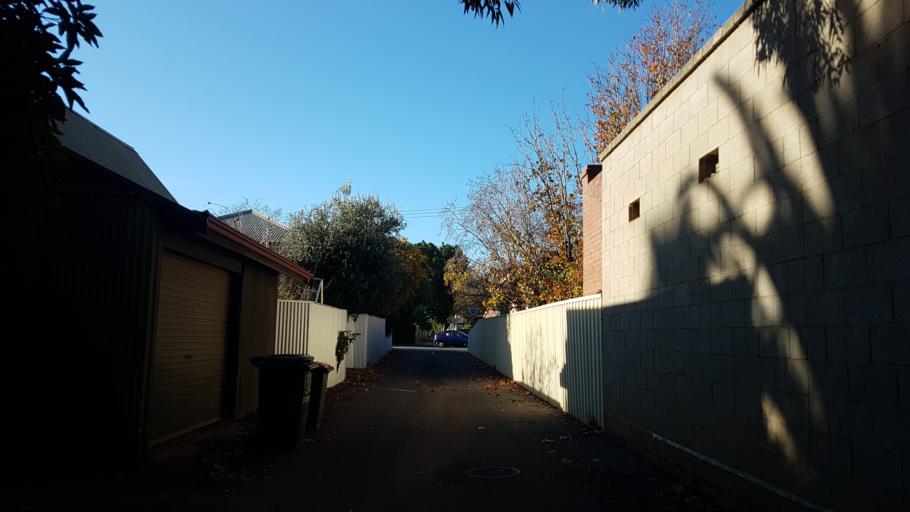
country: AU
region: South Australia
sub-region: Norwood Payneham St Peters
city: Royston Park
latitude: -34.9066
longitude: 138.6246
